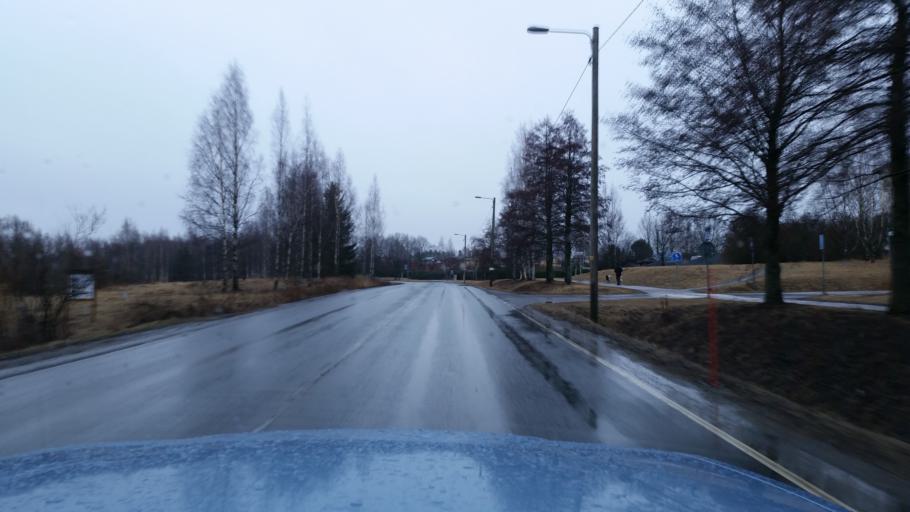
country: FI
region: Pirkanmaa
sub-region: Tampere
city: Tampere
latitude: 61.4811
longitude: 23.8088
